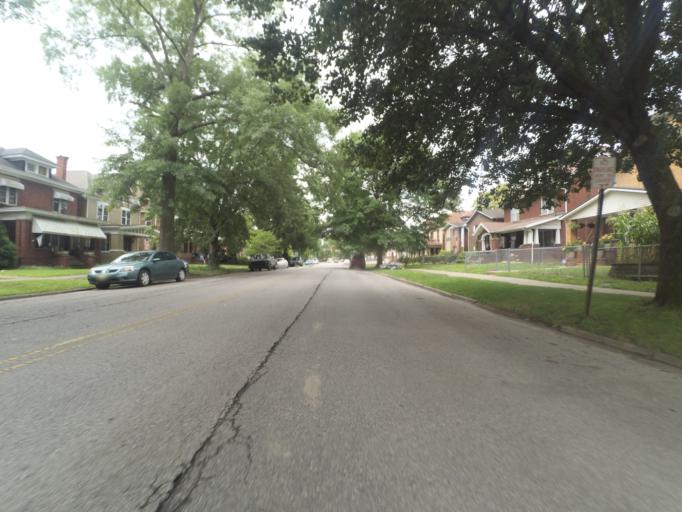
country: US
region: West Virginia
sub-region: Cabell County
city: Huntington
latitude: 38.4143
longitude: -82.4387
